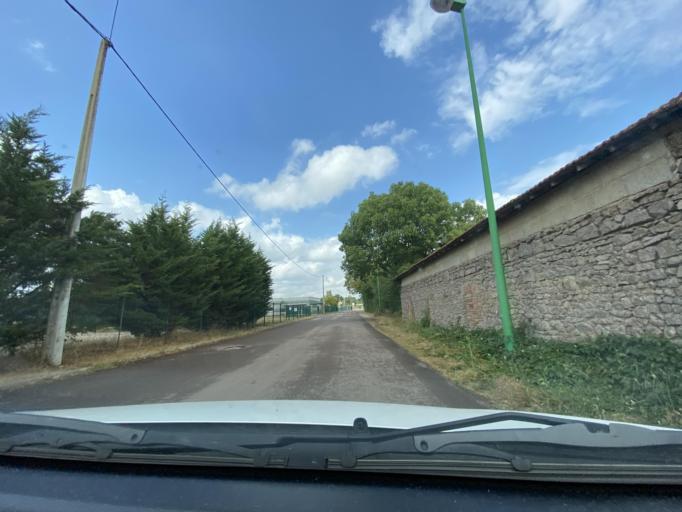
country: FR
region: Bourgogne
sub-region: Departement de la Cote-d'Or
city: Saulieu
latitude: 47.2882
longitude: 4.2320
